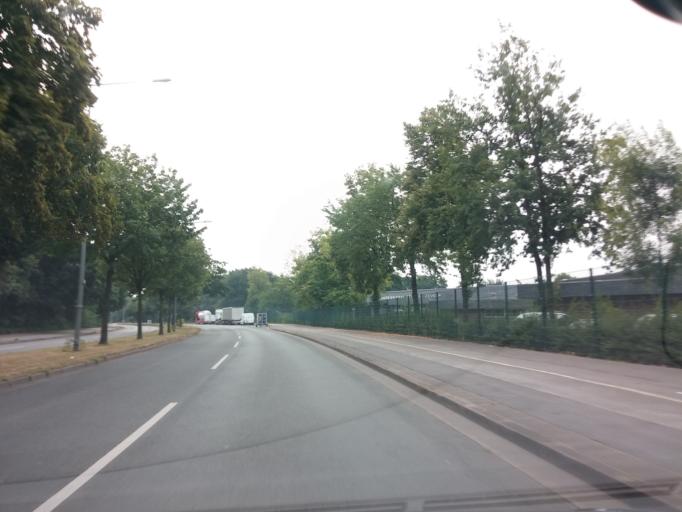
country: DE
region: North Rhine-Westphalia
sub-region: Regierungsbezirk Munster
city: Gelsenkirchen
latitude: 51.5503
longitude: 7.0967
